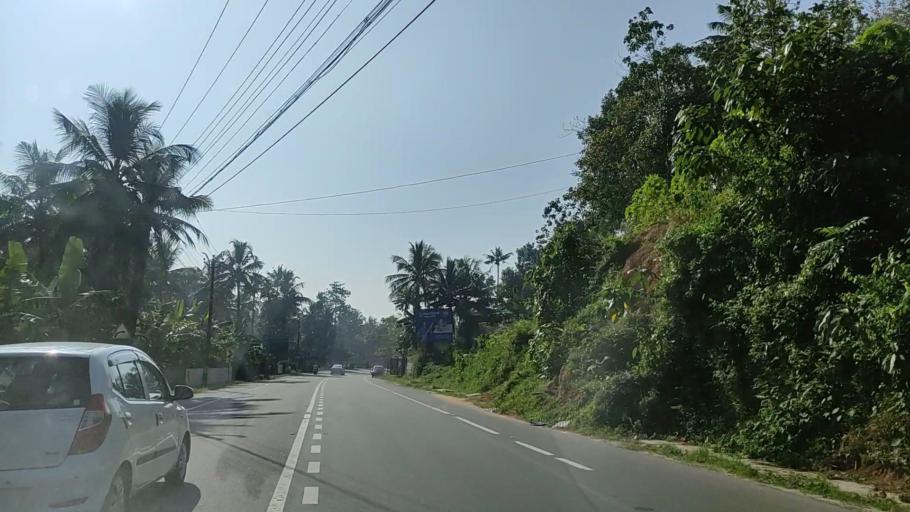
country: IN
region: Kerala
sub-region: Kollam
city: Punalur
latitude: 8.9206
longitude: 76.8548
